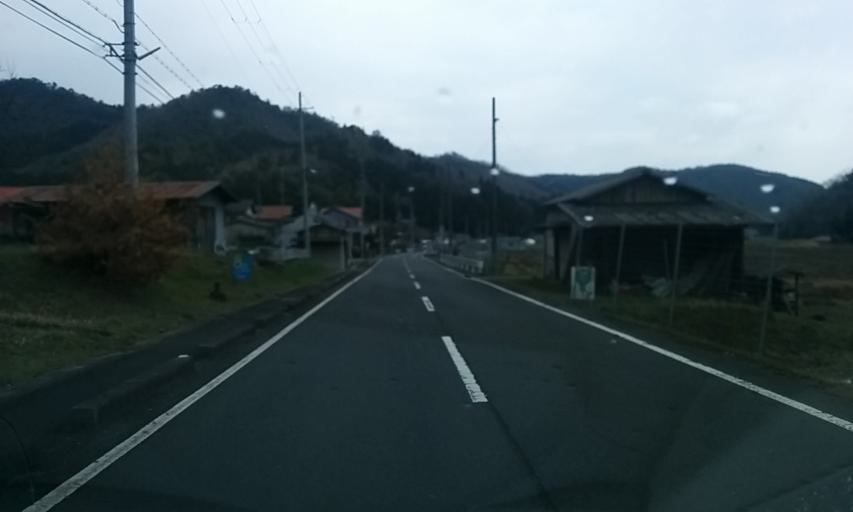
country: JP
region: Hyogo
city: Sasayama
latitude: 35.1284
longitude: 135.4117
